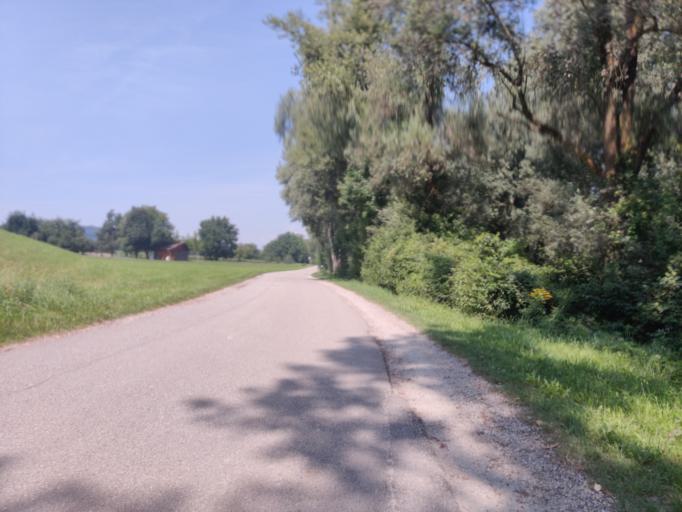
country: AT
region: Upper Austria
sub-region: Politischer Bezirk Urfahr-Umgebung
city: Ottensheim
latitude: 48.3287
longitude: 14.1663
